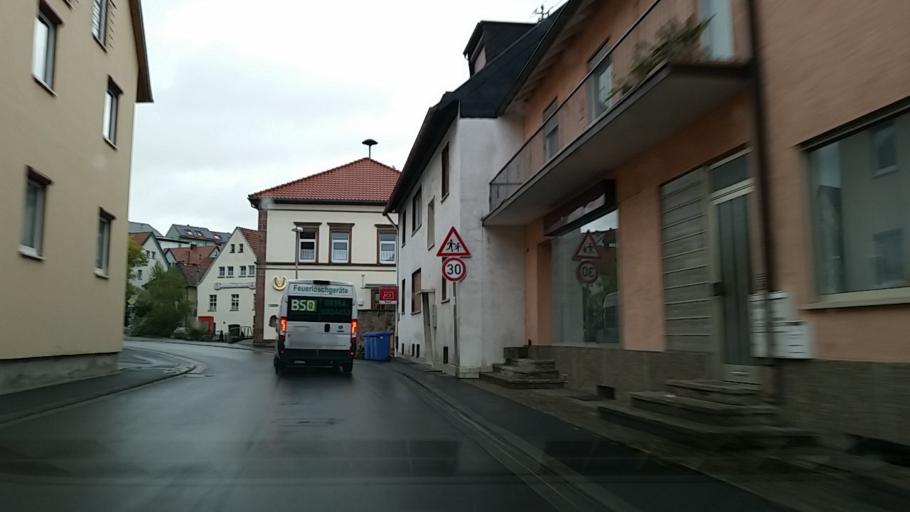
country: DE
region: Bavaria
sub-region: Regierungsbezirk Unterfranken
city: Gossenheim
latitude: 50.0024
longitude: 9.7555
